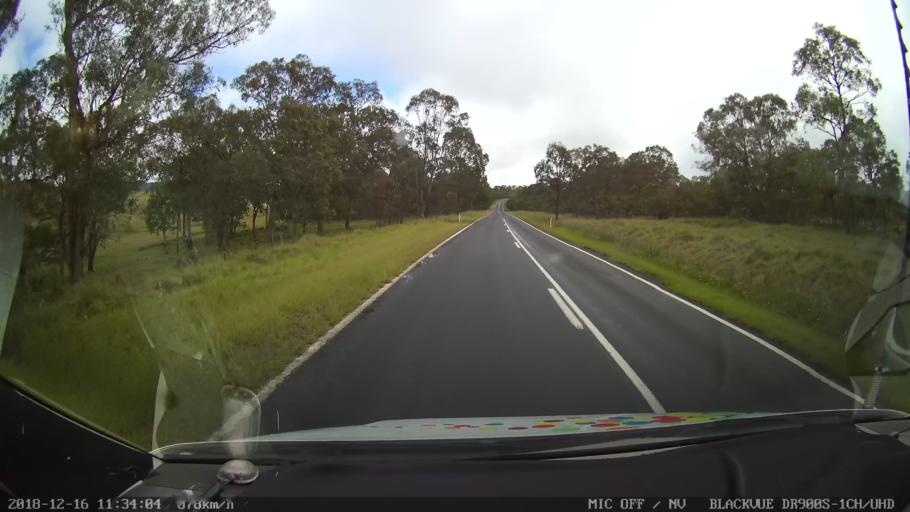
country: AU
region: New South Wales
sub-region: Tenterfield Municipality
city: Carrolls Creek
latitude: -29.0026
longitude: 152.1512
